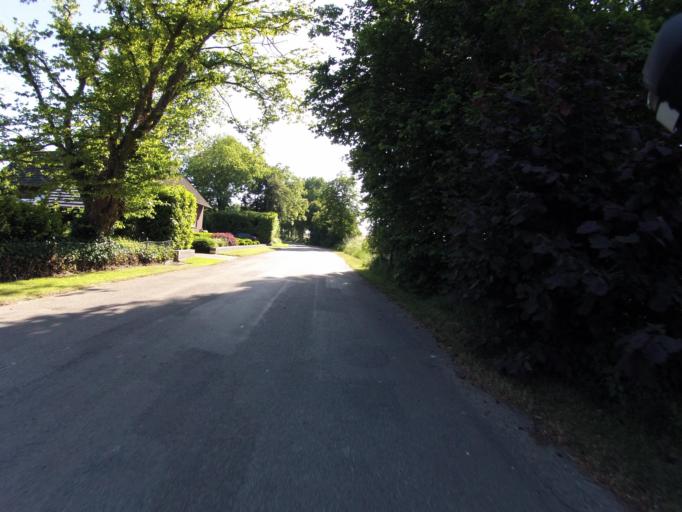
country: DE
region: Lower Saxony
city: Salzbergen
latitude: 52.3081
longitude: 7.3761
